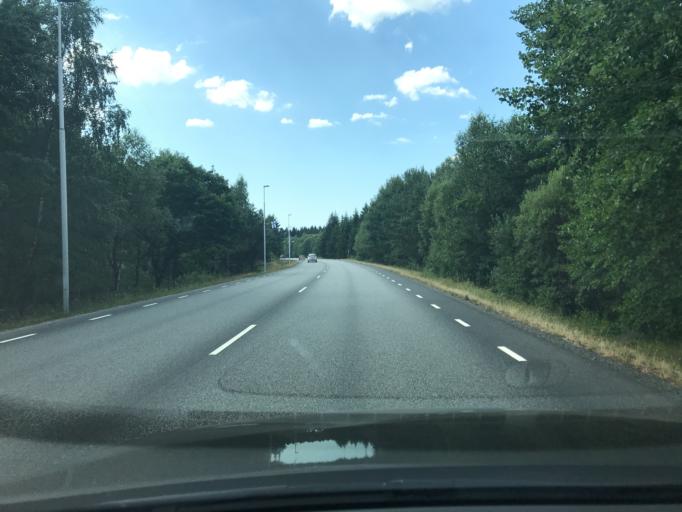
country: SE
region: Skane
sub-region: Hassleholms Kommun
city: Hastveda
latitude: 56.2748
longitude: 13.9488
